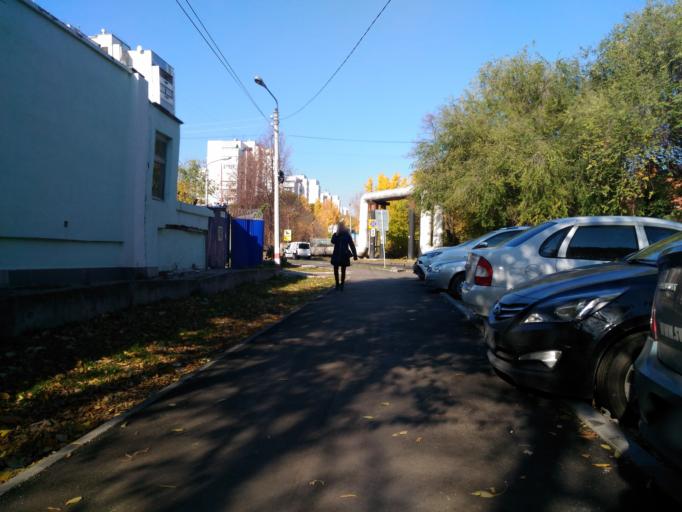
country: RU
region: Ulyanovsk
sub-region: Ulyanovskiy Rayon
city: Ulyanovsk
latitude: 54.3287
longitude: 48.3940
